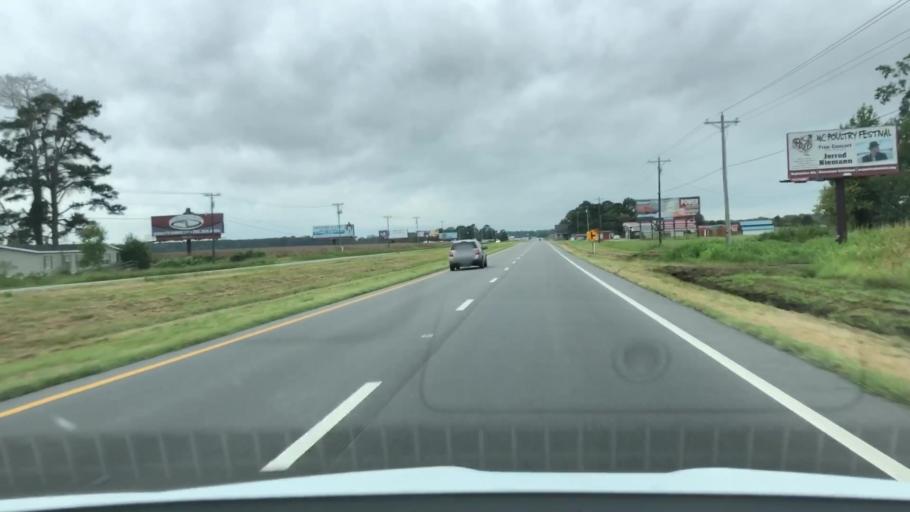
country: US
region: North Carolina
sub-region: Lenoir County
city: La Grange
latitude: 35.2631
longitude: -77.7207
